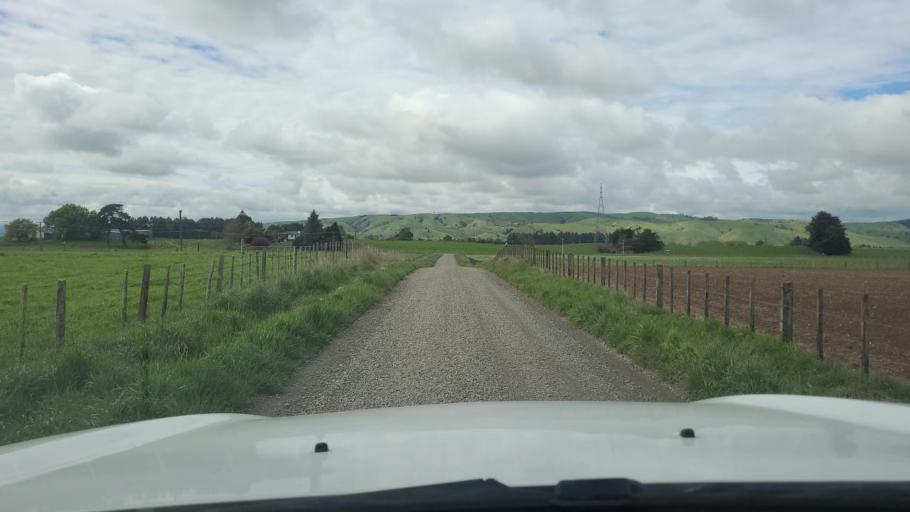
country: NZ
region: Wellington
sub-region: Masterton District
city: Masterton
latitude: -41.1029
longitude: 175.4674
